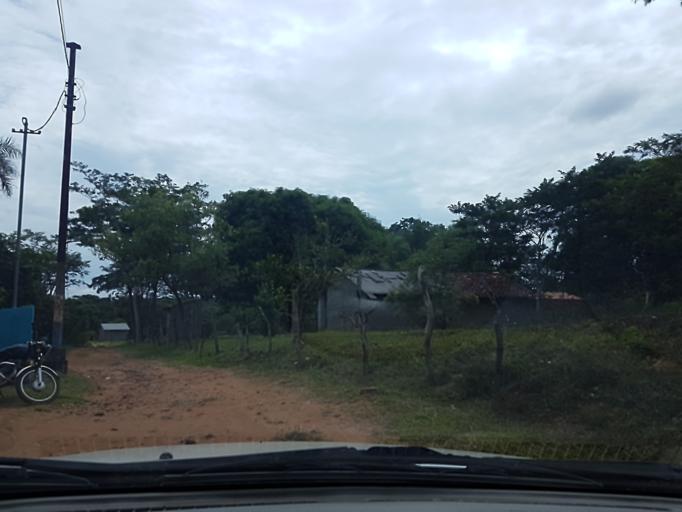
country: PY
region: Central
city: Limpio
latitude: -25.2370
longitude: -57.4460
